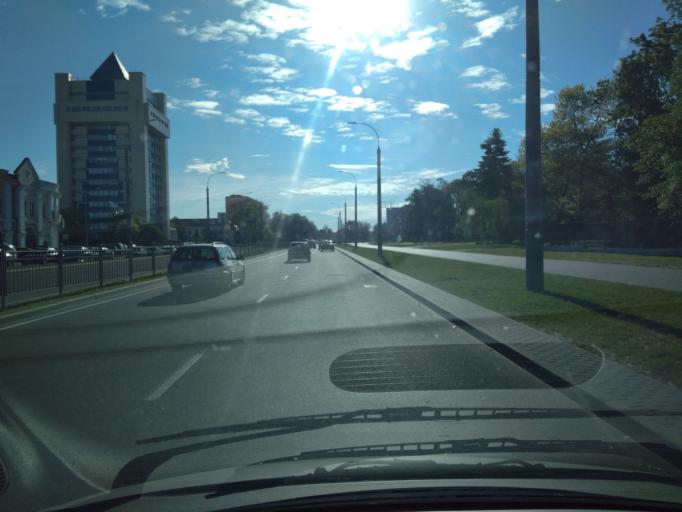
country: BY
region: Brest
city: Brest
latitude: 52.0859
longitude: 23.6832
